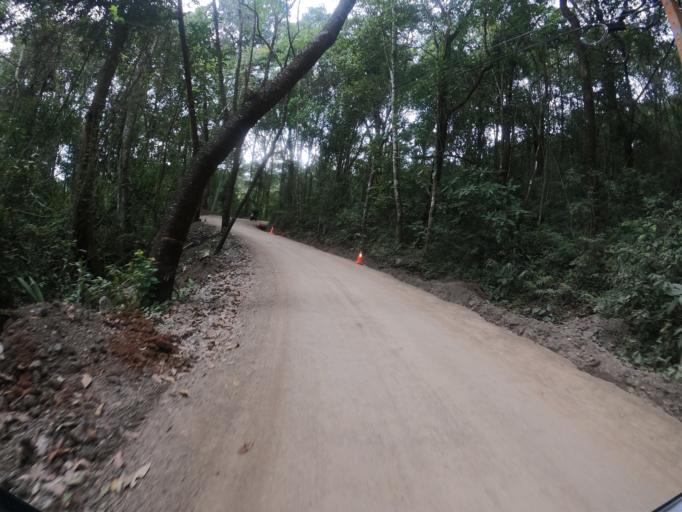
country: TH
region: Chiang Mai
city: Chiang Mai
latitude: 18.8132
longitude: 98.8907
